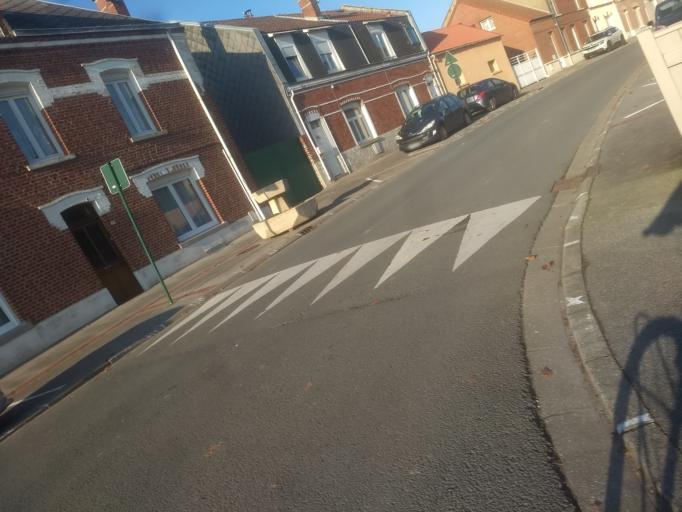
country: FR
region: Nord-Pas-de-Calais
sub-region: Departement du Pas-de-Calais
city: Tilloy-les-Mofflaines
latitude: 50.2751
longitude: 2.8168
